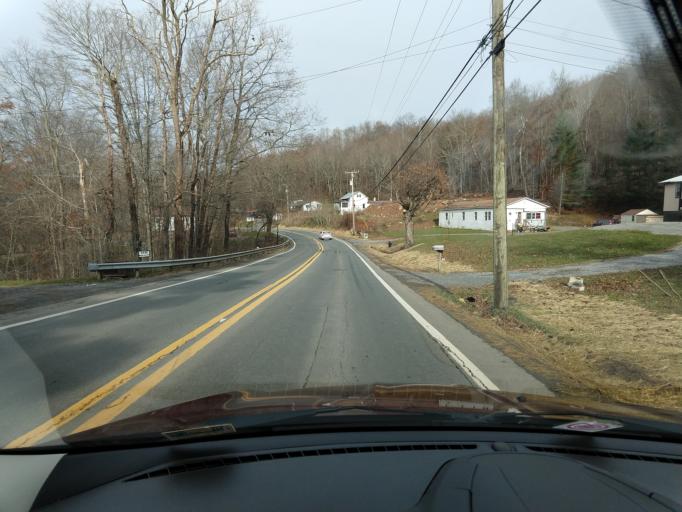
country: US
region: West Virginia
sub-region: Greenbrier County
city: Rainelle
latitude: 37.9676
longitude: -80.7003
